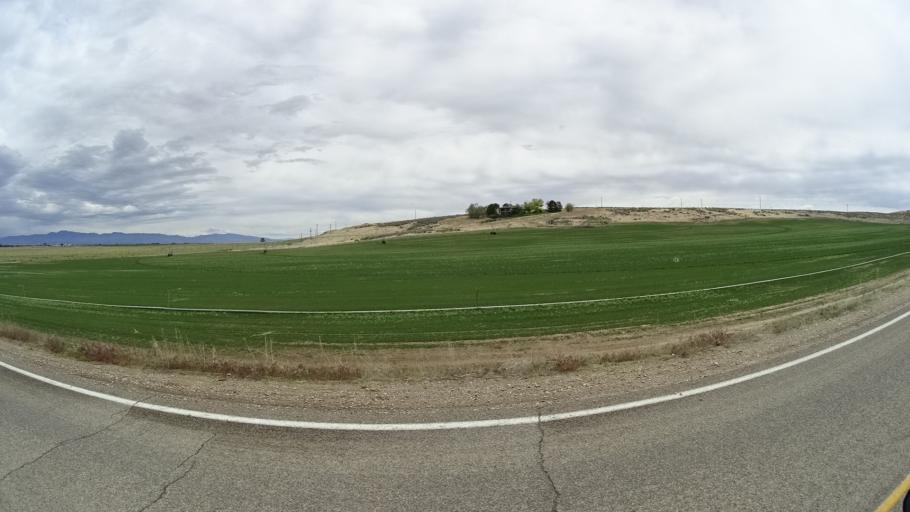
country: US
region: Idaho
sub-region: Ada County
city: Kuna
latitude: 43.4616
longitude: -116.4440
